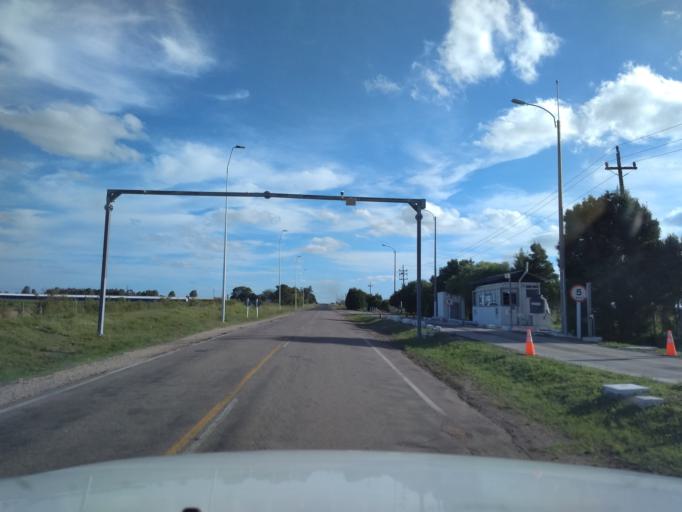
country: UY
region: Canelones
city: San Ramon
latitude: -34.2444
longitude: -55.9255
